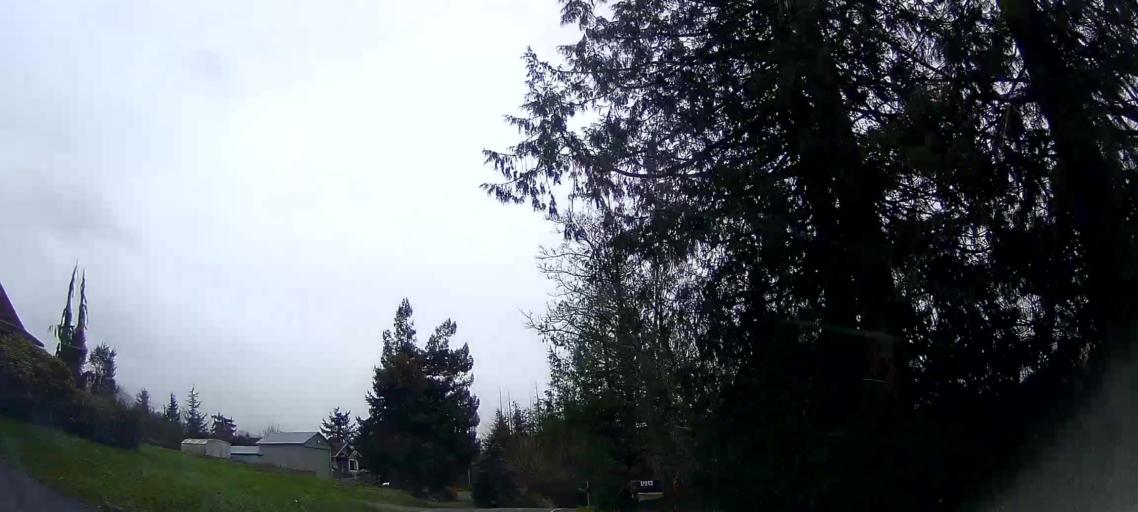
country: US
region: Washington
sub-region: Skagit County
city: Mount Vernon
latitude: 48.3857
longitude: -122.3218
